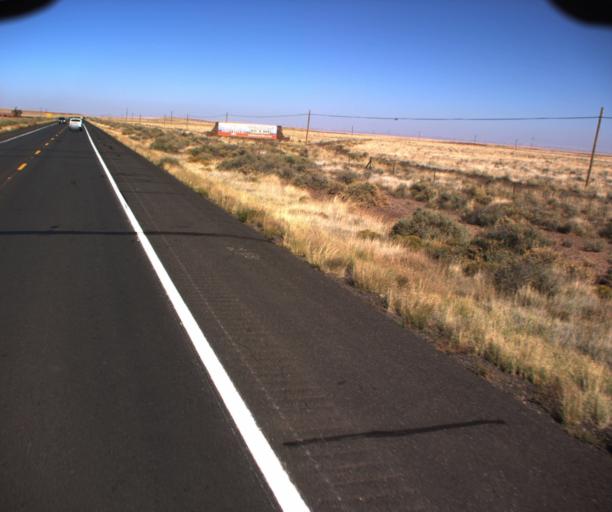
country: US
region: Arizona
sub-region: Coconino County
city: Flagstaff
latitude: 35.6805
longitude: -111.5073
